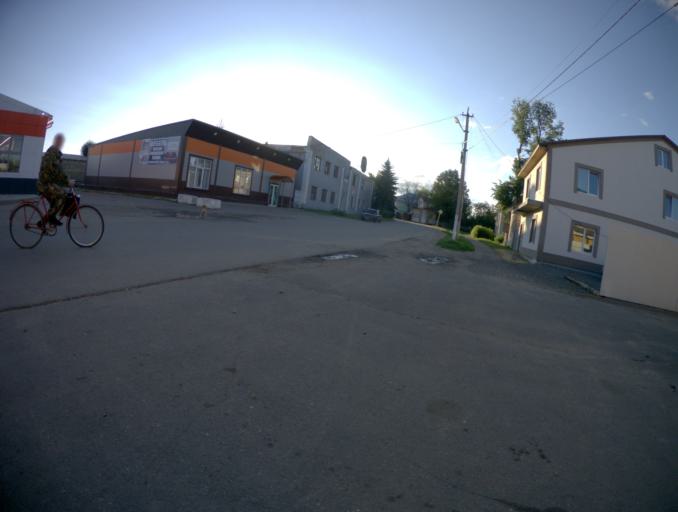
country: RU
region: Ivanovo
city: Gavrilov Posad
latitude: 56.5593
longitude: 40.1203
